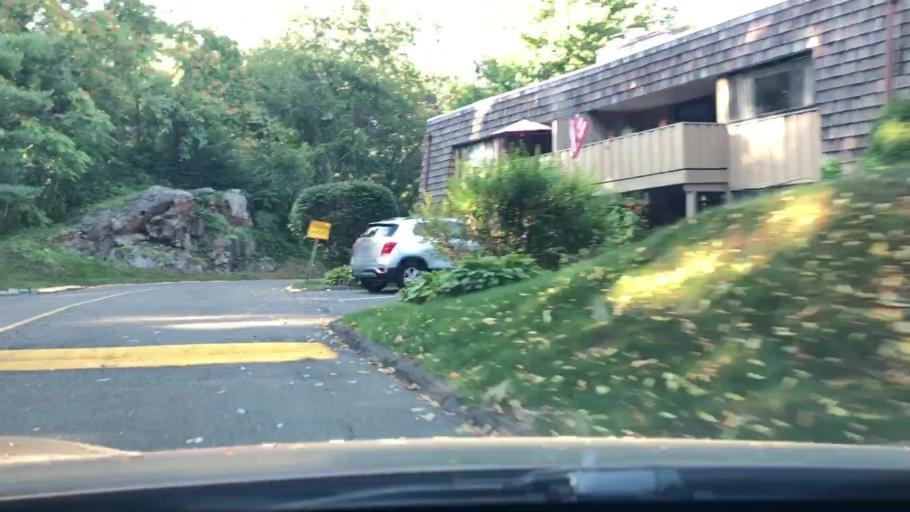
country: US
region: Connecticut
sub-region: Fairfield County
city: Norwalk
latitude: 41.1078
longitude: -73.4405
